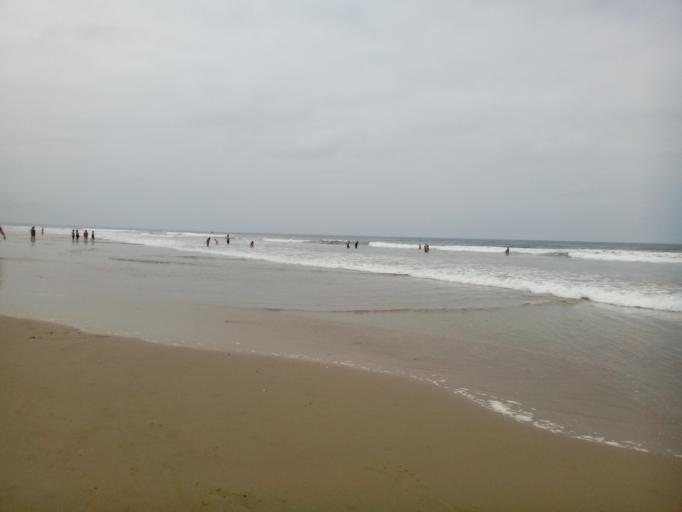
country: EC
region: Santa Elena
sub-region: Canton Santa Elena
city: Santa Elena
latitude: -1.8266
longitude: -80.7543
